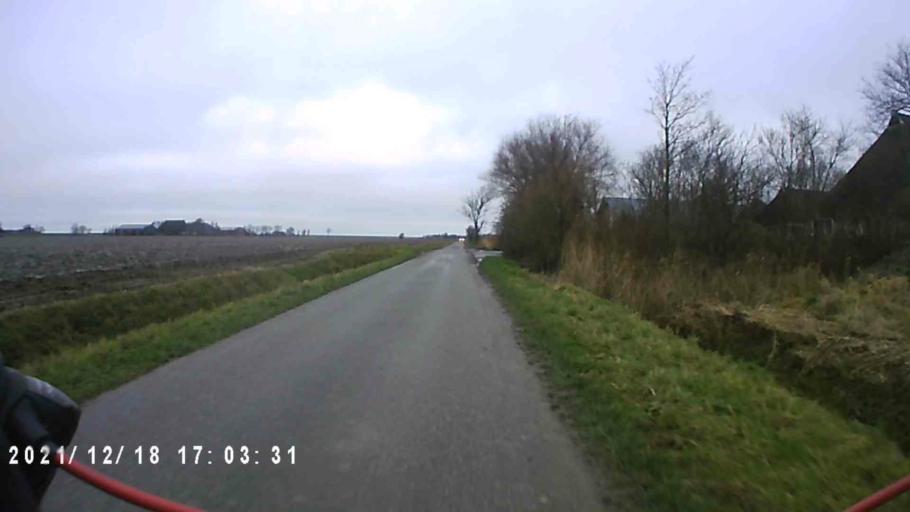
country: NL
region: Friesland
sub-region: Gemeente Dongeradeel
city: Holwerd
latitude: 53.3716
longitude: 5.9226
